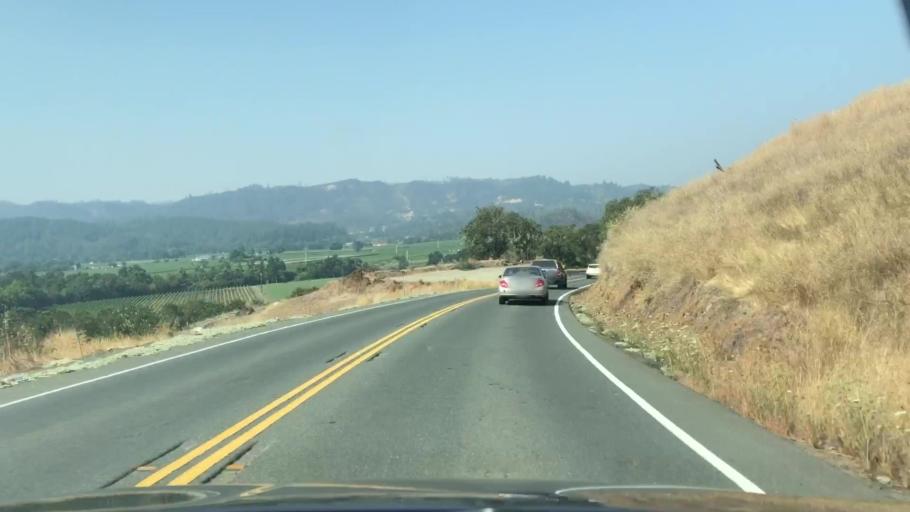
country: US
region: California
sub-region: Napa County
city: Calistoga
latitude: 38.6075
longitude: -122.5964
